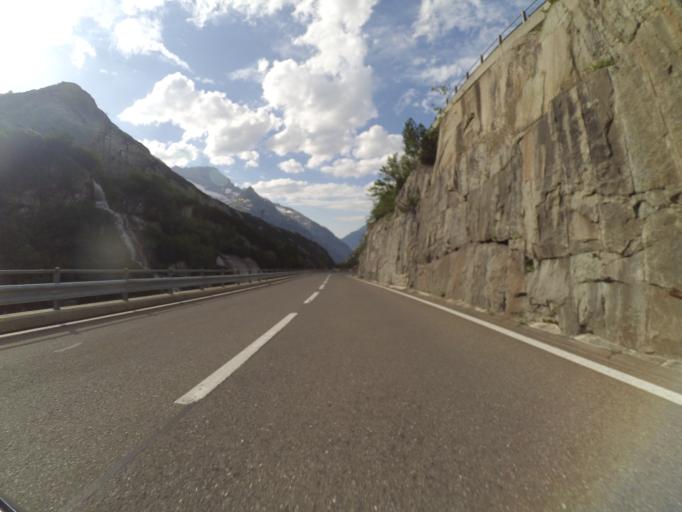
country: CH
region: Bern
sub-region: Interlaken-Oberhasli District
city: Meiringen
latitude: 46.5917
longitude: 8.3244
